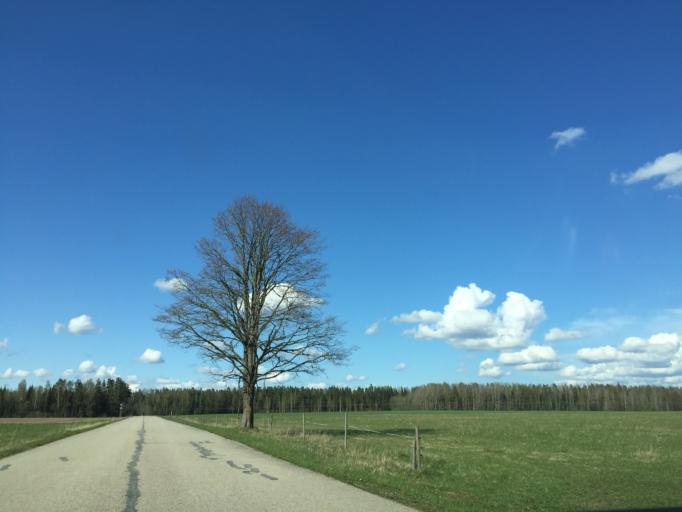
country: LV
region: Beverina
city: Murmuiza
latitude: 57.4921
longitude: 25.5692
